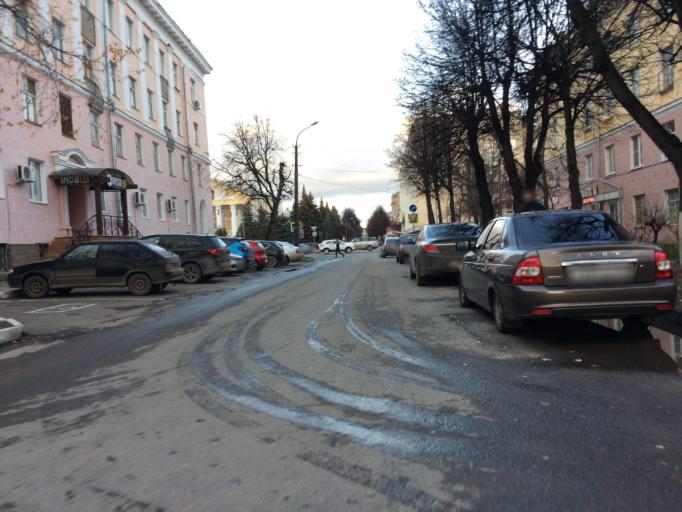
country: RU
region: Mariy-El
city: Yoshkar-Ola
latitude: 56.6296
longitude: 47.8911
